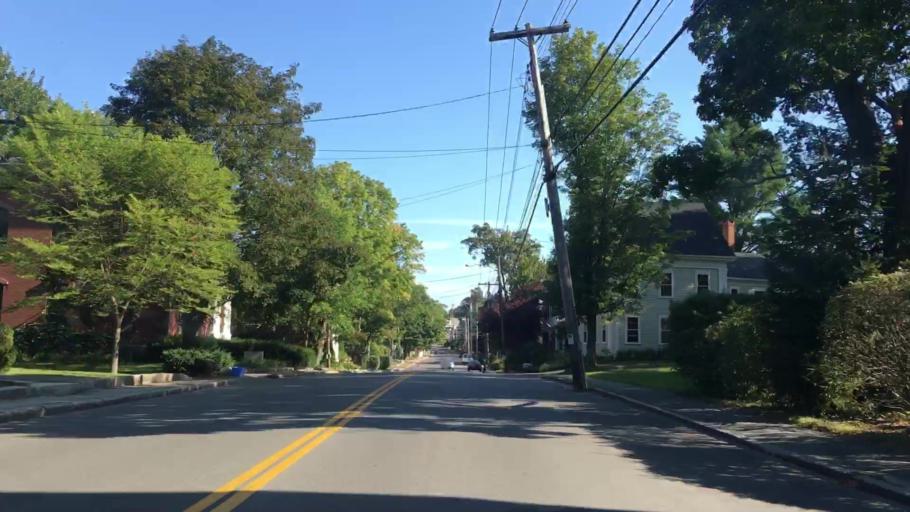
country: US
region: Maine
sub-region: Sagadahoc County
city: Bath
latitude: 43.9200
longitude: -69.8150
